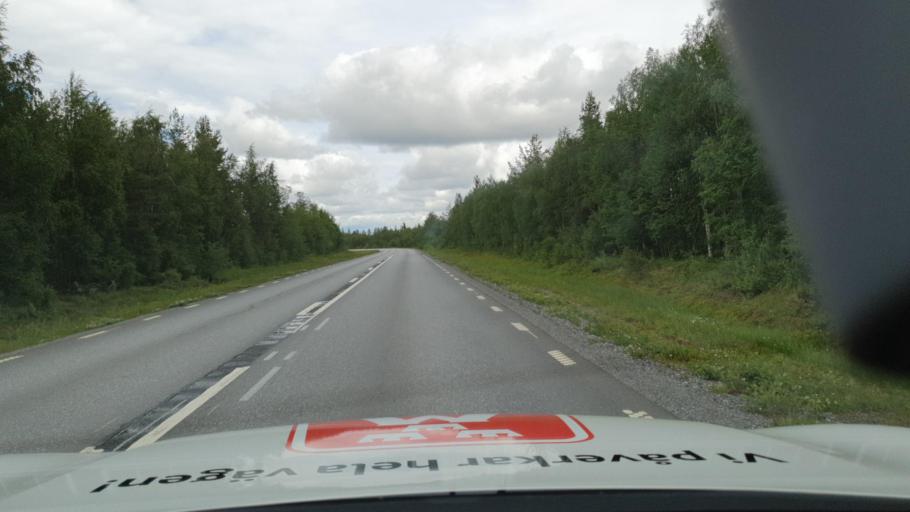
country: SE
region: Vaesterbotten
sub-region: Dorotea Kommun
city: Dorotea
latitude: 64.3329
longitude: 16.6368
